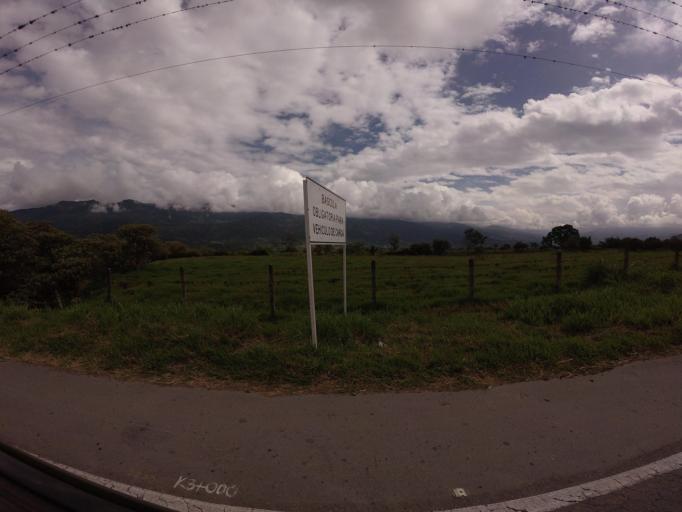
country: CO
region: Cundinamarca
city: Fusagasuga
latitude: 4.3430
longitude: -74.4072
